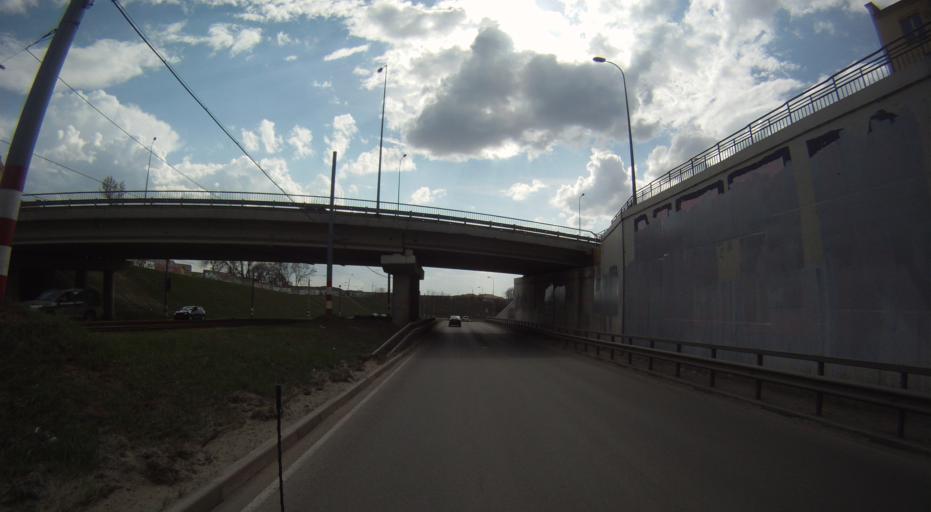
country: RU
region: Nizjnij Novgorod
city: Nizhniy Novgorod
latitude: 56.3048
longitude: 43.9785
